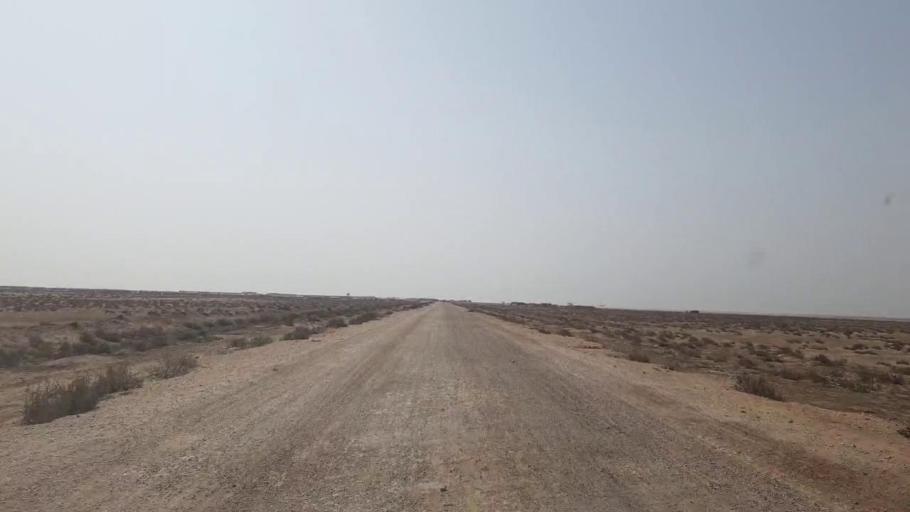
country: PK
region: Sindh
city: Jati
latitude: 24.3491
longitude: 68.5936
